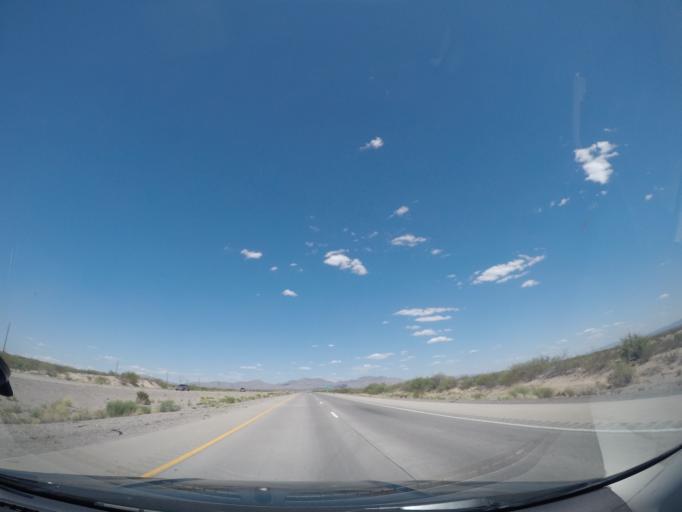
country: US
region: Texas
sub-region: Hudspeth County
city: Fort Hancock
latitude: 31.1736
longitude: -105.6786
